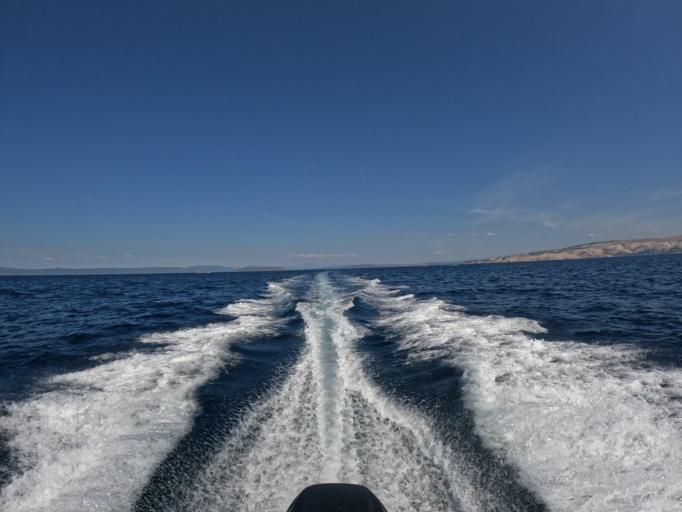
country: HR
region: Primorsko-Goranska
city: Lopar
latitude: 44.8953
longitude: 14.6405
